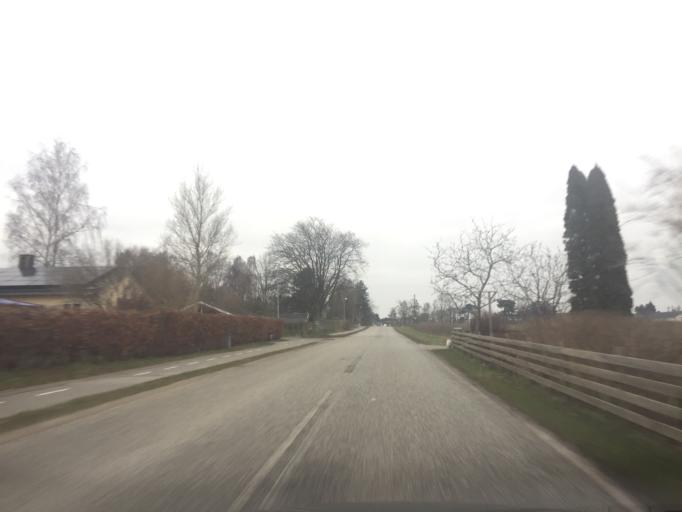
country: DK
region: Capital Region
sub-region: Halsnaes Kommune
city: Liseleje
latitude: 55.9831
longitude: 11.9796
